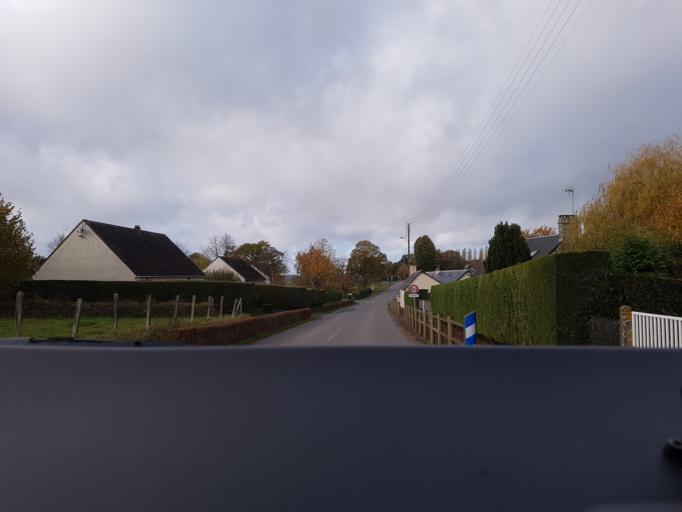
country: FR
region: Lower Normandy
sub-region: Departement de l'Orne
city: Ceauce
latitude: 48.4870
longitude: -0.5813
